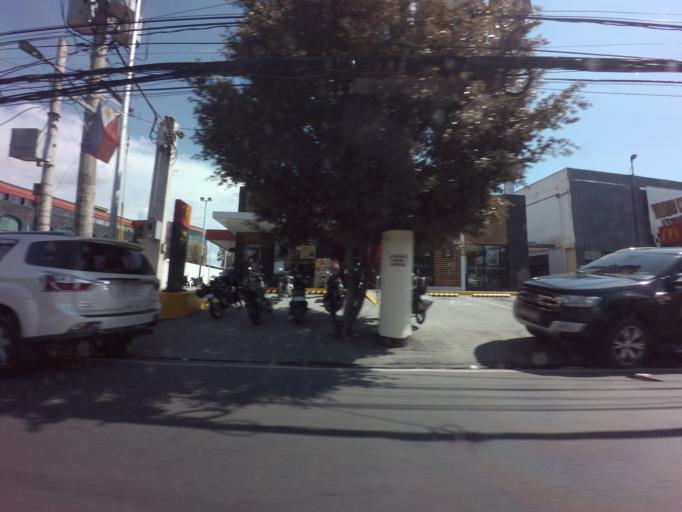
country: PH
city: Sambayanihan People's Village
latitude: 14.4414
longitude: 120.9983
